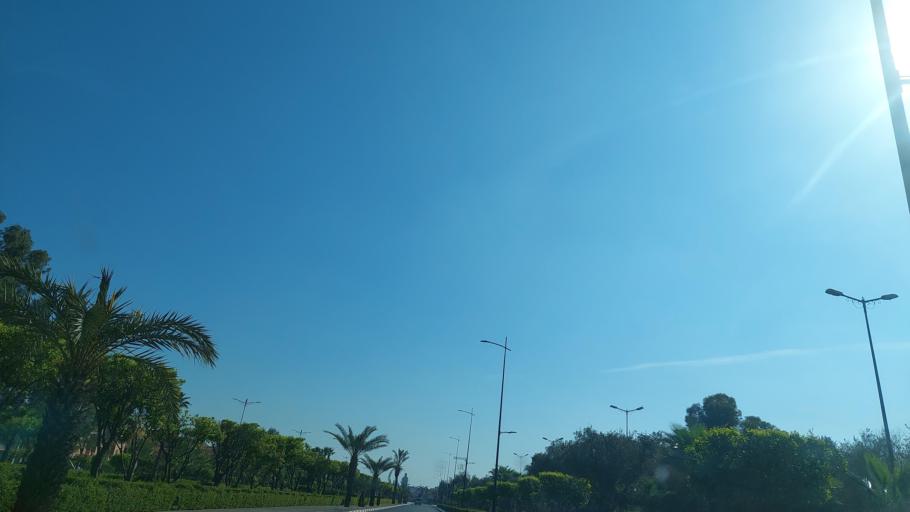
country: MA
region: Marrakech-Tensift-Al Haouz
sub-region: Marrakech
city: Marrakesh
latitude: 31.6008
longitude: -7.9692
